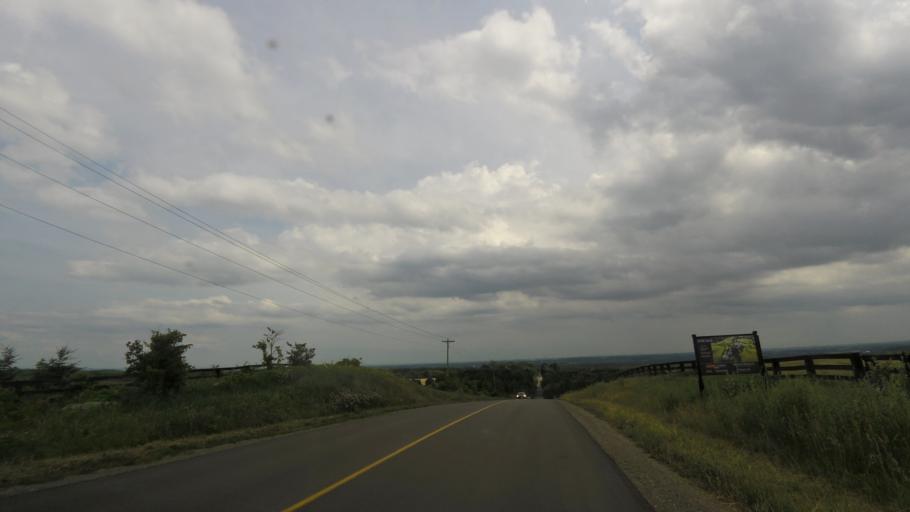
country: CA
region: Ontario
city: Orangeville
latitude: 43.8682
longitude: -79.9352
